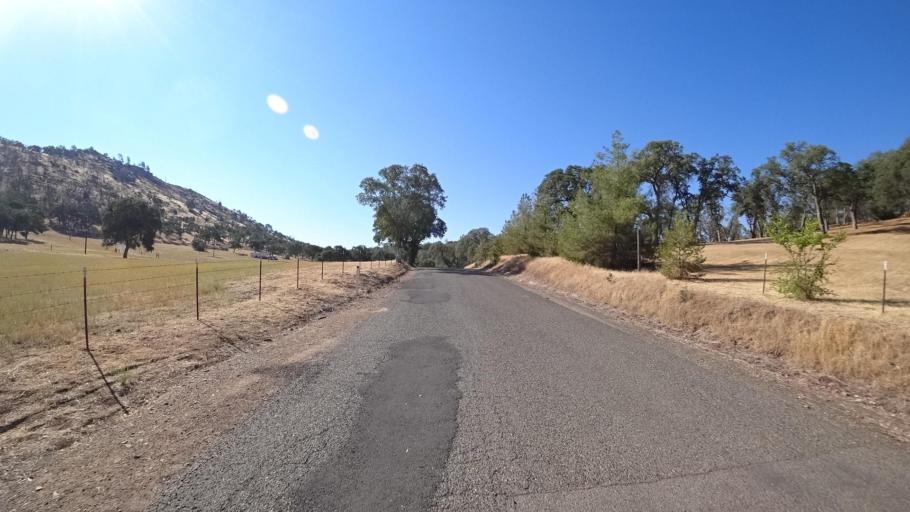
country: US
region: California
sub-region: Mariposa County
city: Mariposa
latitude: 37.6014
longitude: -120.1921
